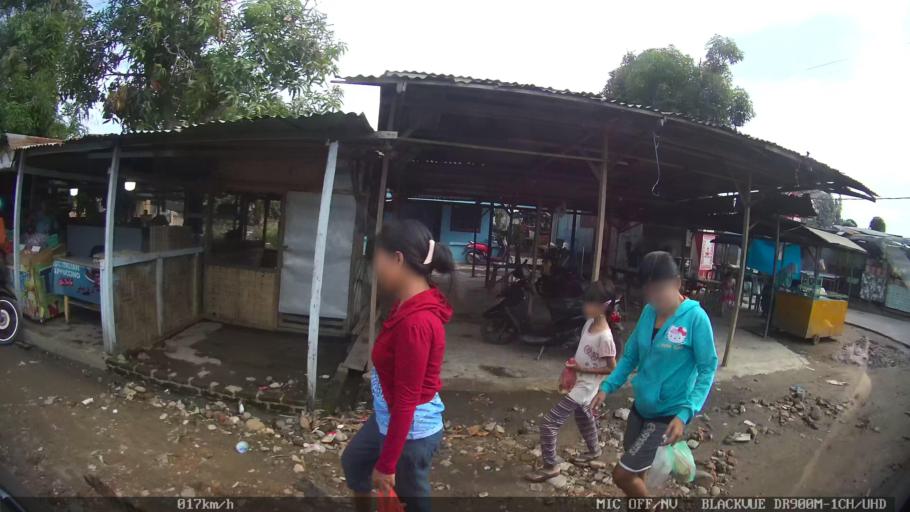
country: ID
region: North Sumatra
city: Medan
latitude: 3.6211
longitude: 98.7219
